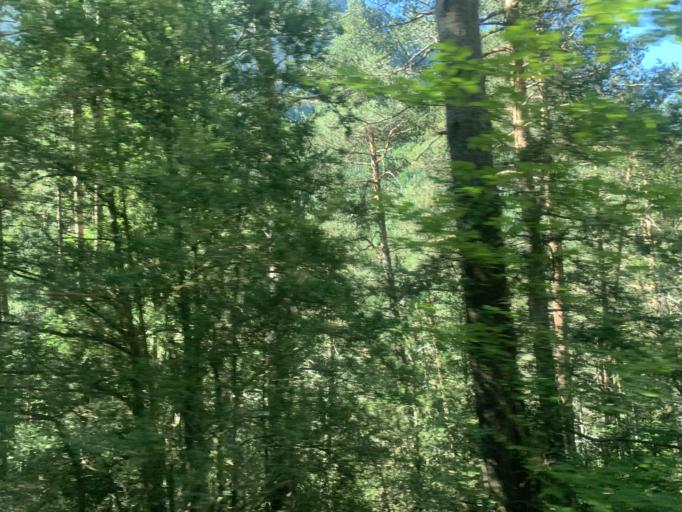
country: ES
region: Aragon
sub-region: Provincia de Huesca
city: Broto
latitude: 42.6552
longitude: -0.0810
